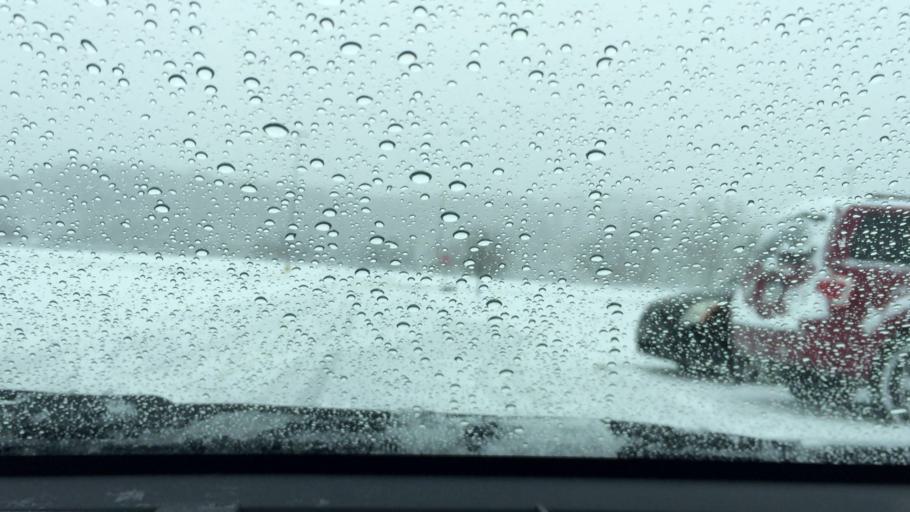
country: US
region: Pennsylvania
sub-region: Allegheny County
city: West View
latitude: 40.5418
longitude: -80.0093
